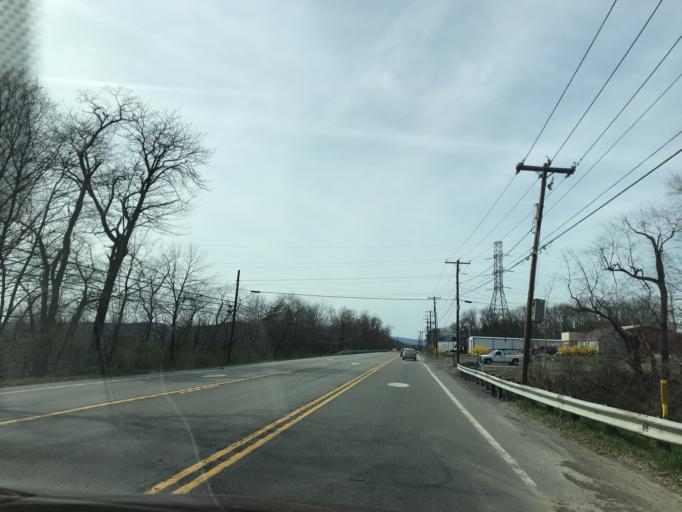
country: US
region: Pennsylvania
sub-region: Northumberland County
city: Northumberland
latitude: 40.9030
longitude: -76.8259
